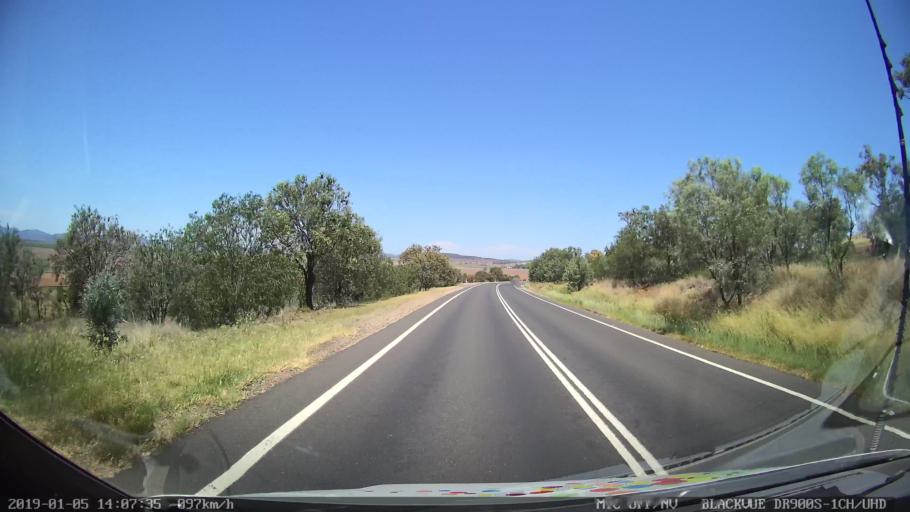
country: AU
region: New South Wales
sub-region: Gunnedah
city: Gunnedah
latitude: -31.2238
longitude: 150.4084
